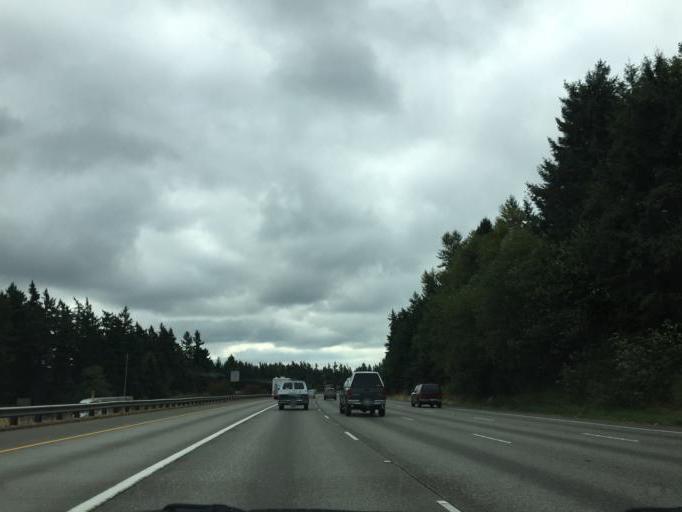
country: US
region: Washington
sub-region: King County
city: Lakeland North
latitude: 47.3480
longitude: -122.2939
